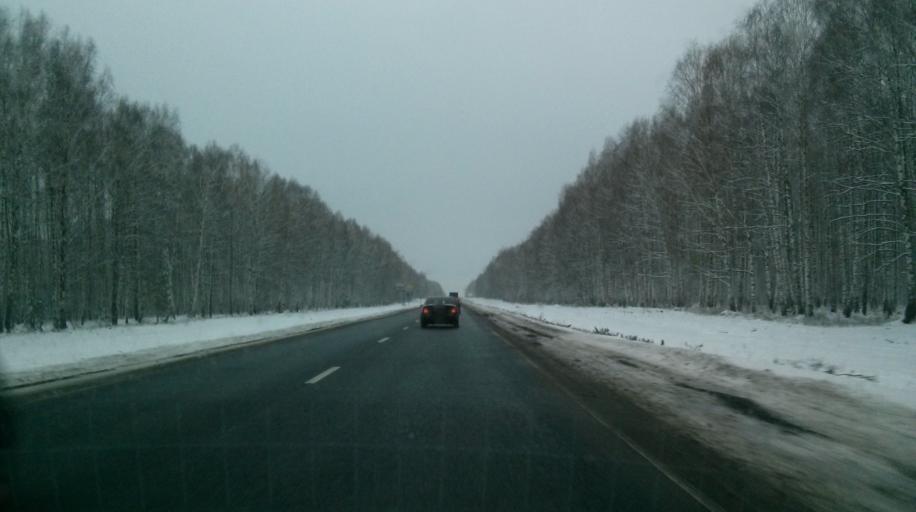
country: RU
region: Nizjnij Novgorod
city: Vorsma
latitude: 56.0095
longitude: 43.3340
